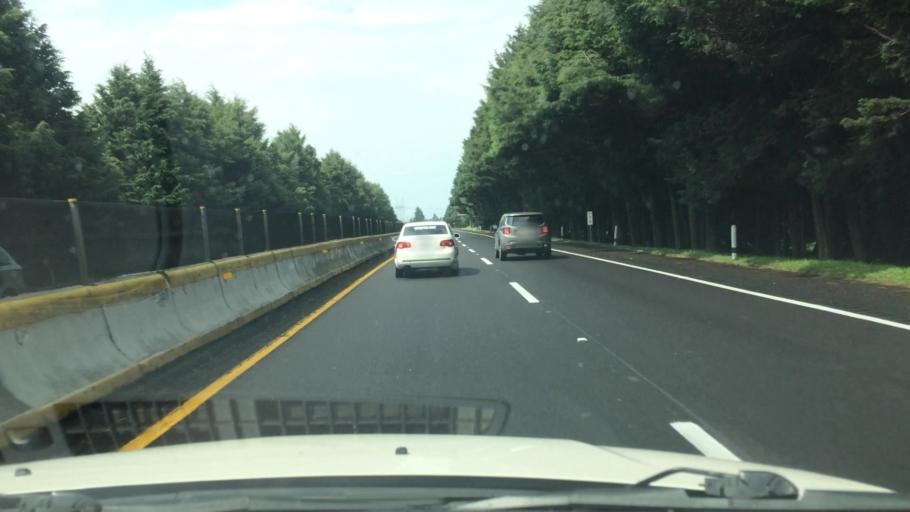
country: MX
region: Mexico City
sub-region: Tlalpan
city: Lomas de Tepemecatl
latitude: 19.1474
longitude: -99.1610
